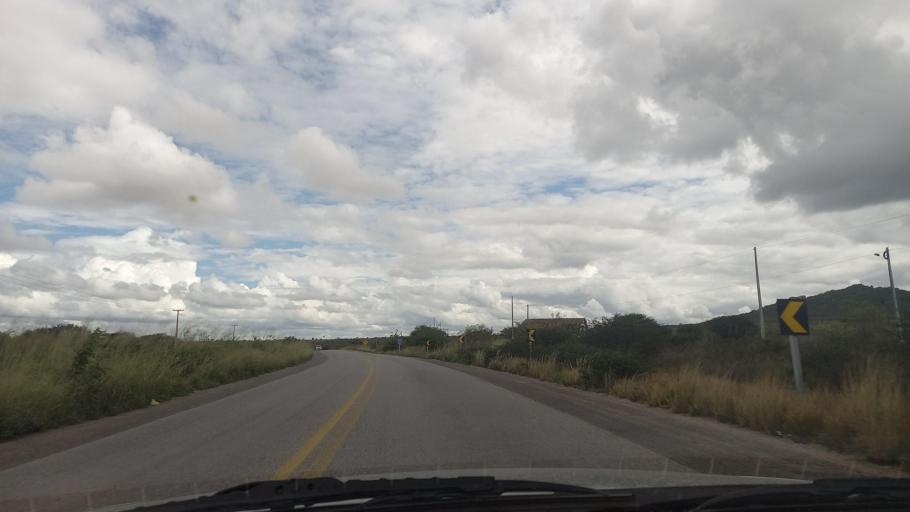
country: BR
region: Pernambuco
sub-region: Cachoeirinha
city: Cachoeirinha
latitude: -8.3503
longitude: -36.1697
